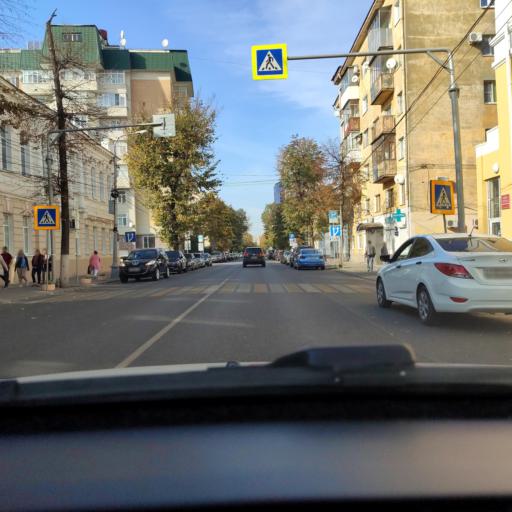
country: RU
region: Voronezj
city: Voronezh
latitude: 51.6592
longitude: 39.2090
